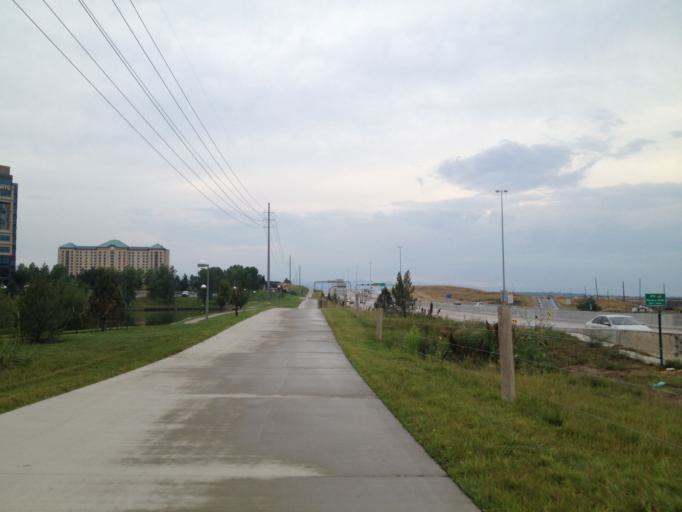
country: US
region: Colorado
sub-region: Broomfield County
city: Broomfield
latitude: 39.9249
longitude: -105.1121
